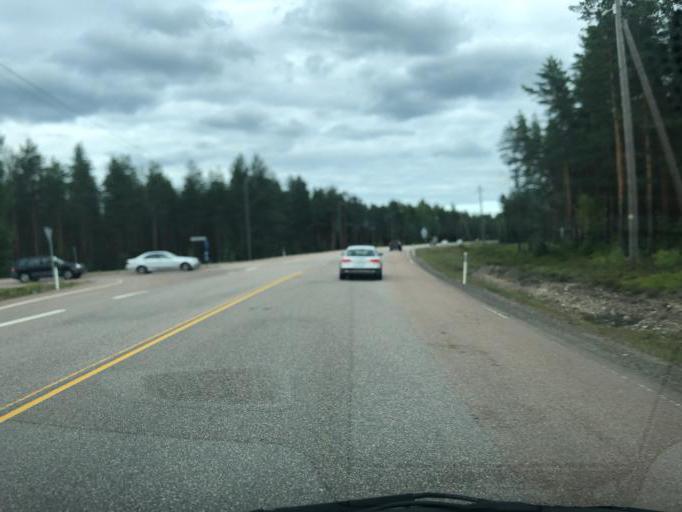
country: FI
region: Southern Savonia
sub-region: Mikkeli
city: Maentyharju
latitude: 61.0909
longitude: 27.0683
